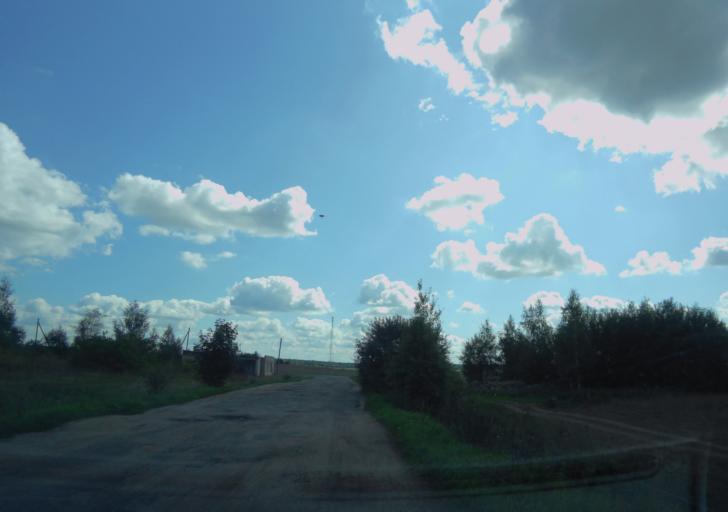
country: BY
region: Minsk
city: Zyembin
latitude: 54.4062
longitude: 28.4005
